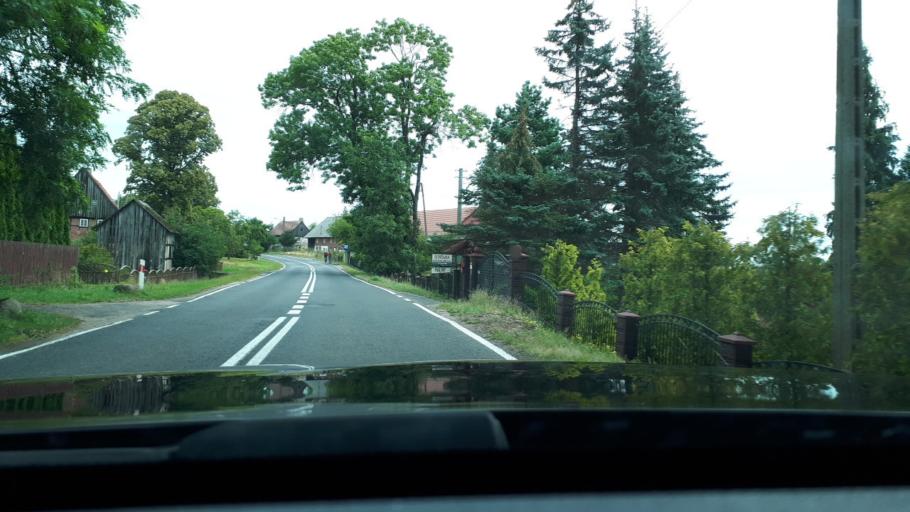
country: PL
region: Lower Silesian Voivodeship
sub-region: Powiat lwowecki
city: Lubomierz
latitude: 51.0925
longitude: 15.4797
